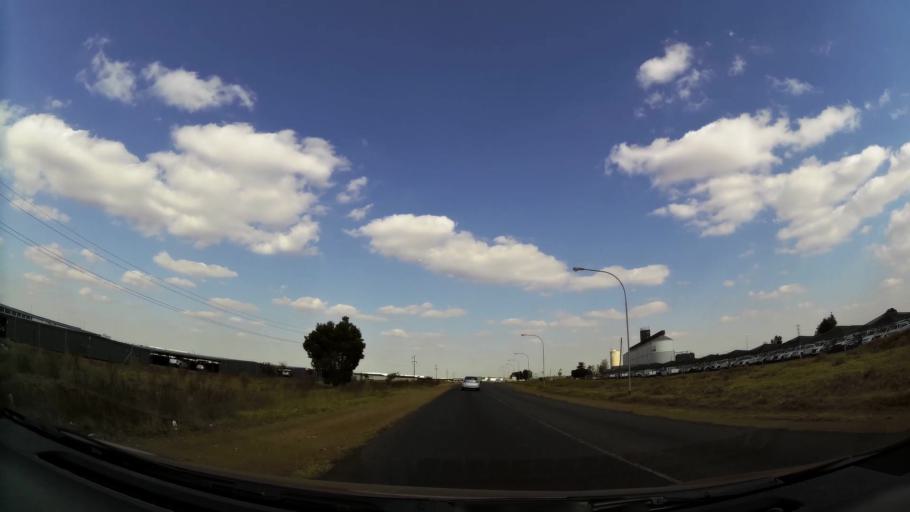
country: ZA
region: Gauteng
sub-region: Ekurhuleni Metropolitan Municipality
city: Tembisa
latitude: -26.0219
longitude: 28.2580
